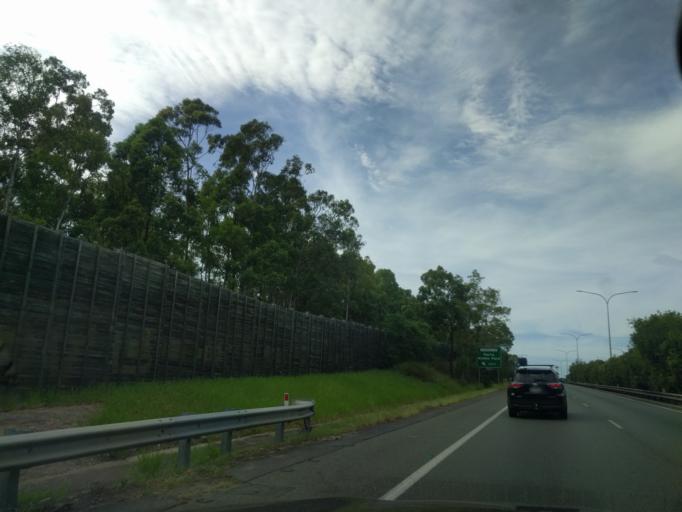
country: AU
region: Queensland
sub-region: Brisbane
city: Seventeen Mile Rocks
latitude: -27.5546
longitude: 152.9406
